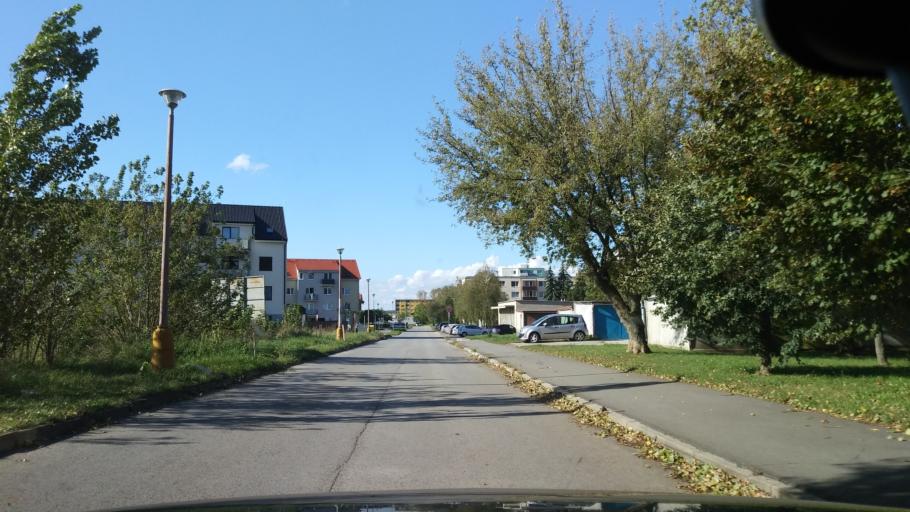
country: SK
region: Trnavsky
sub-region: Okres Skalica
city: Skalica
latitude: 48.8365
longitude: 17.2250
